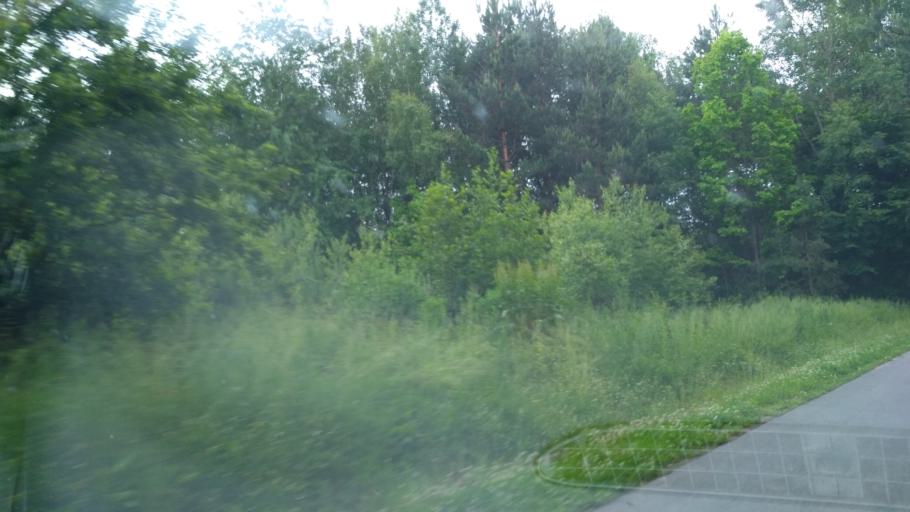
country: PL
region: Subcarpathian Voivodeship
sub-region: Powiat przemyski
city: Przedmiescie Dubieckie
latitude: 49.8737
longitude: 22.4045
